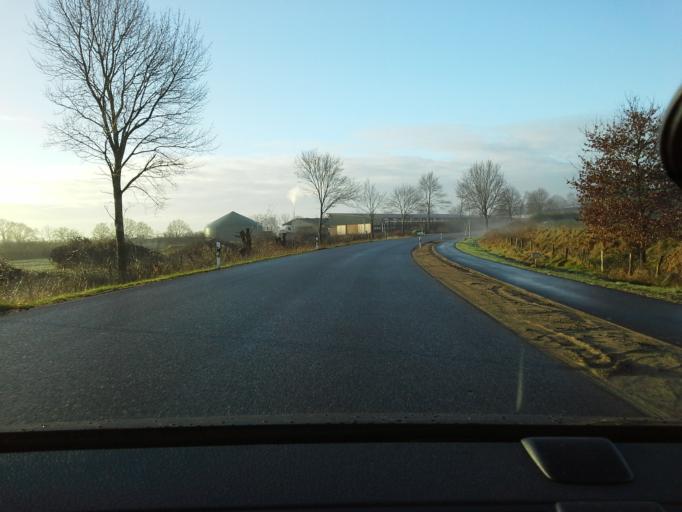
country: DE
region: Schleswig-Holstein
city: Borstel-Hohenraden
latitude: 53.6909
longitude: 9.8178
